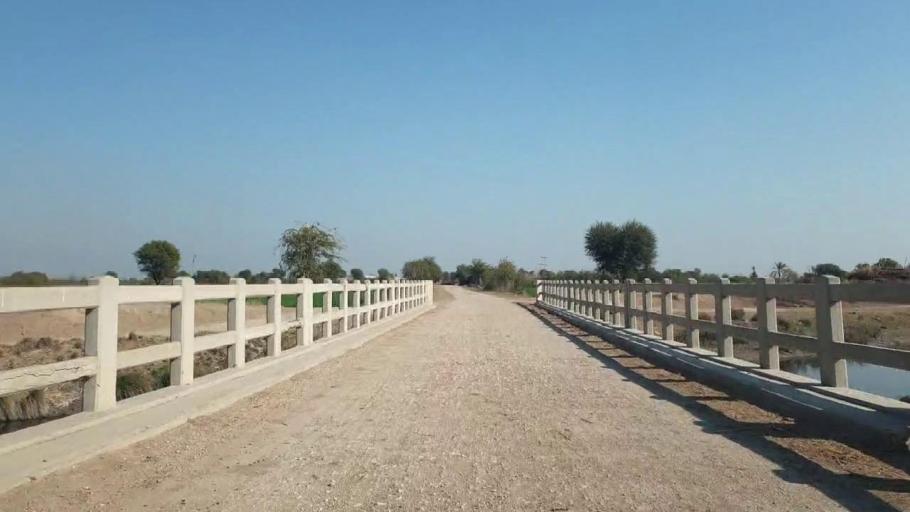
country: PK
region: Sindh
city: Shahdadpur
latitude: 25.9789
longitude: 68.6627
